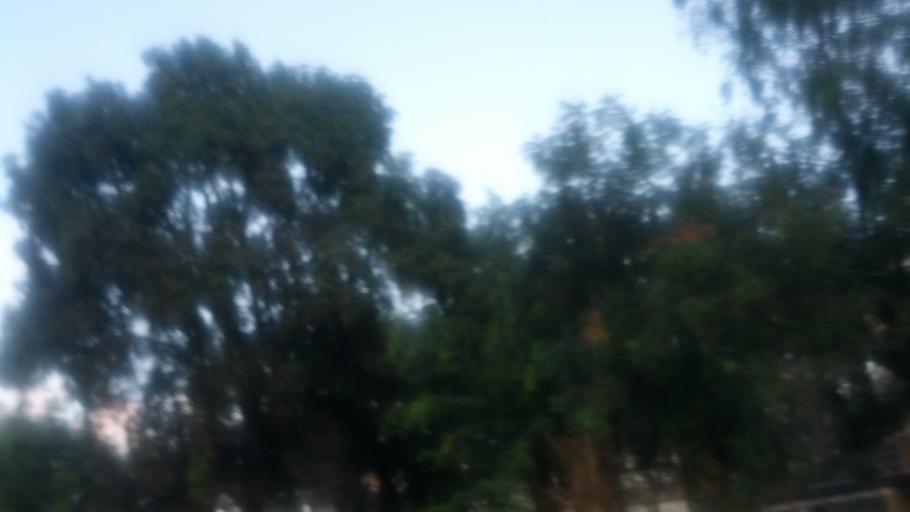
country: CI
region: Vallee du Bandama
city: Bouake
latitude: 7.6880
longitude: -5.0583
